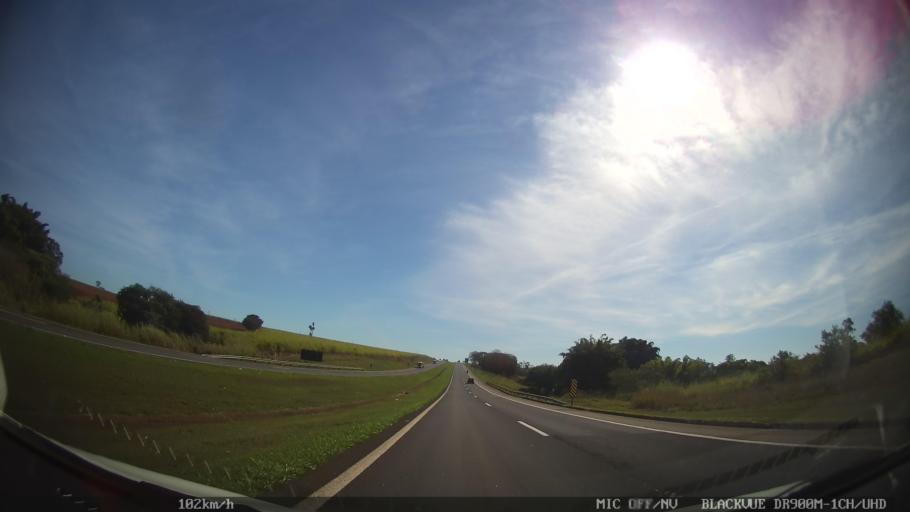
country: BR
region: Sao Paulo
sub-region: Leme
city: Leme
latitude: -22.1159
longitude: -47.4118
